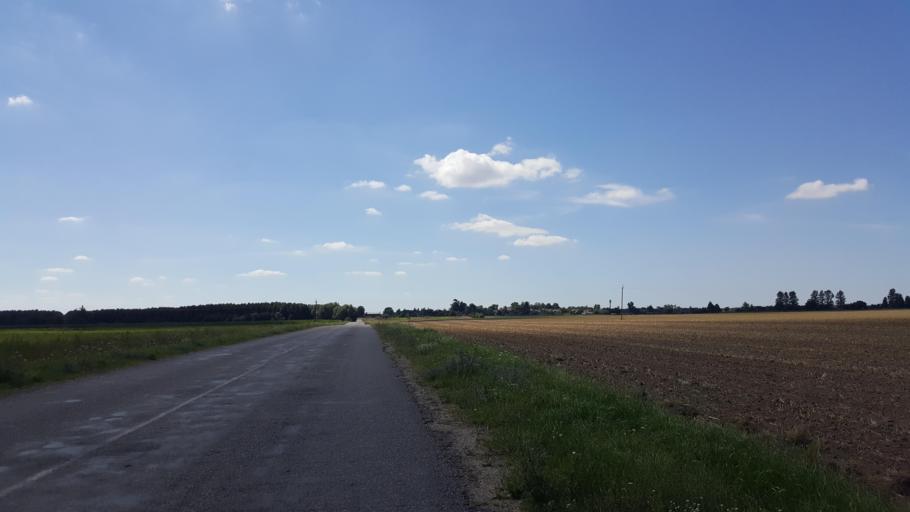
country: BY
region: Brest
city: Charnawchytsy
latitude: 52.3539
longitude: 23.6165
